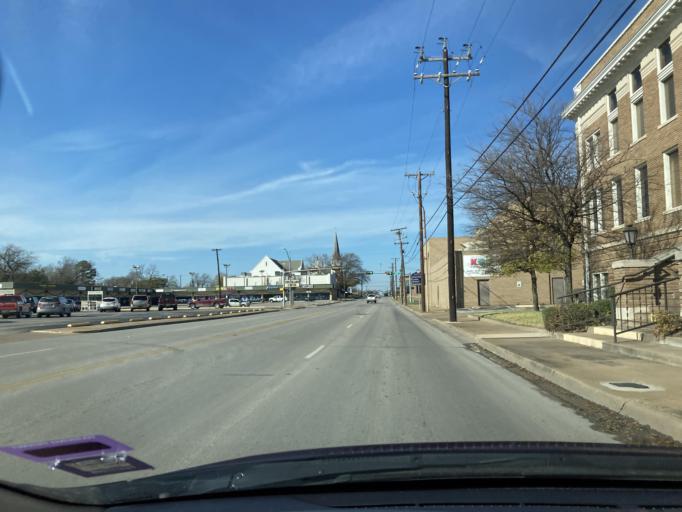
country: US
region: Texas
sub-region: Navarro County
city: Corsicana
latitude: 32.0911
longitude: -96.4691
